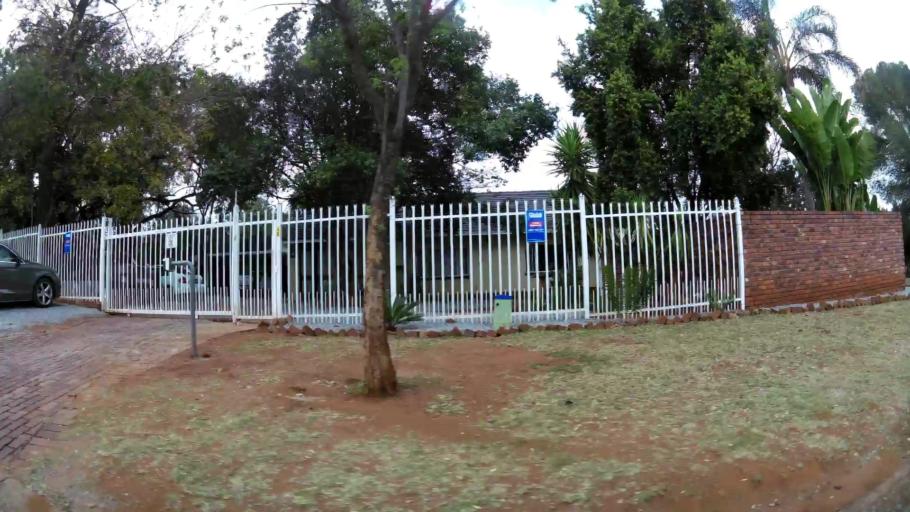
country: ZA
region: Gauteng
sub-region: City of Tshwane Metropolitan Municipality
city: Pretoria
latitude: -25.7502
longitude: 28.3061
